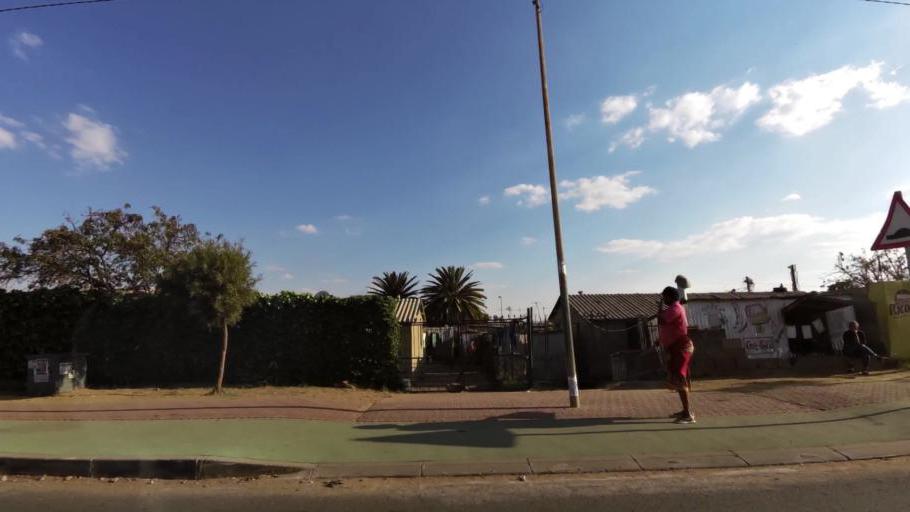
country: ZA
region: Gauteng
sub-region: City of Johannesburg Metropolitan Municipality
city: Soweto
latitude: -26.2197
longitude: 27.8873
